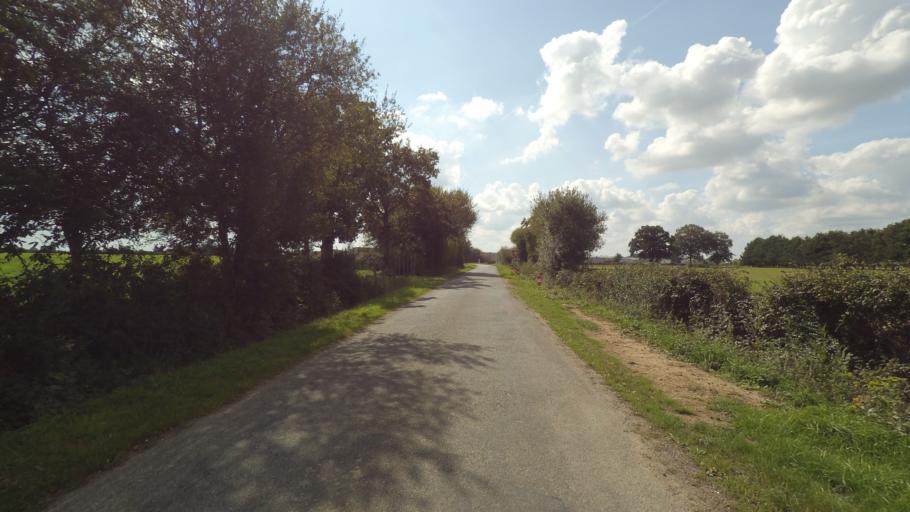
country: FR
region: Pays de la Loire
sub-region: Departement de la Loire-Atlantique
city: Vieillevigne
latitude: 46.9734
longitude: -1.4063
